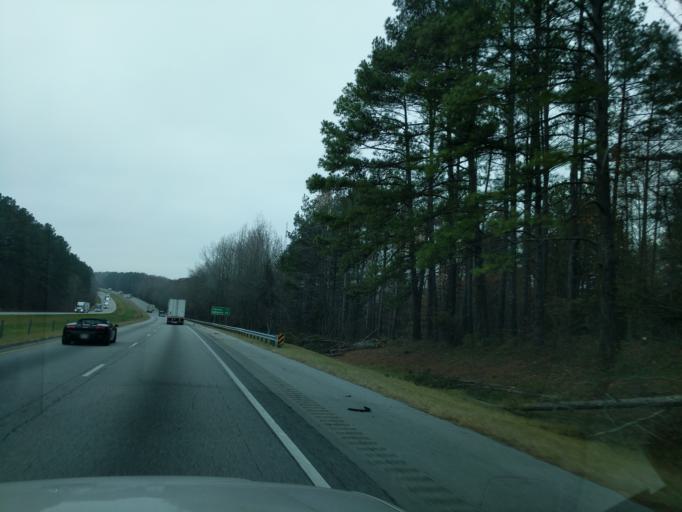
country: US
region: Georgia
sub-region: Franklin County
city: Gumlog
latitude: 34.4666
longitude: -83.0816
